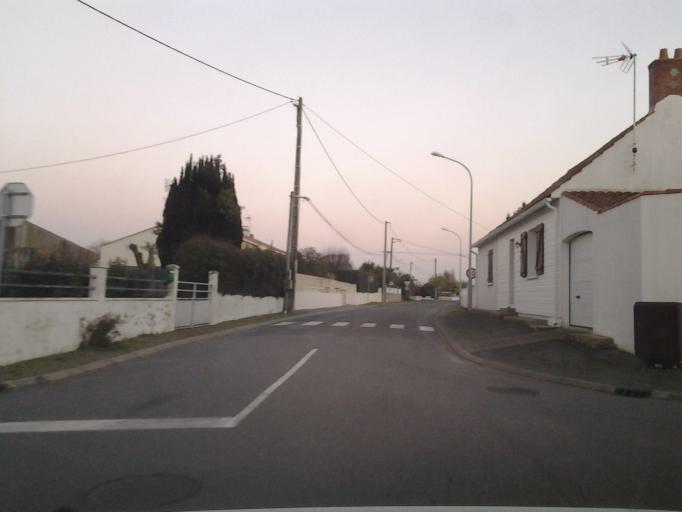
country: FR
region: Pays de la Loire
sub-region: Departement de la Vendee
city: Beauvoir-sur-Mer
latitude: 46.9124
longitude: -2.0406
